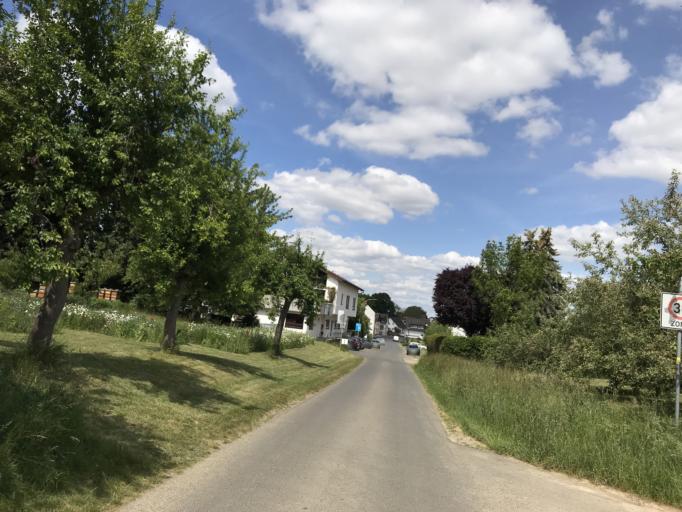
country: DE
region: Hesse
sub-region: Regierungsbezirk Darmstadt
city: Ober-Morlen
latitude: 50.4002
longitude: 8.6721
